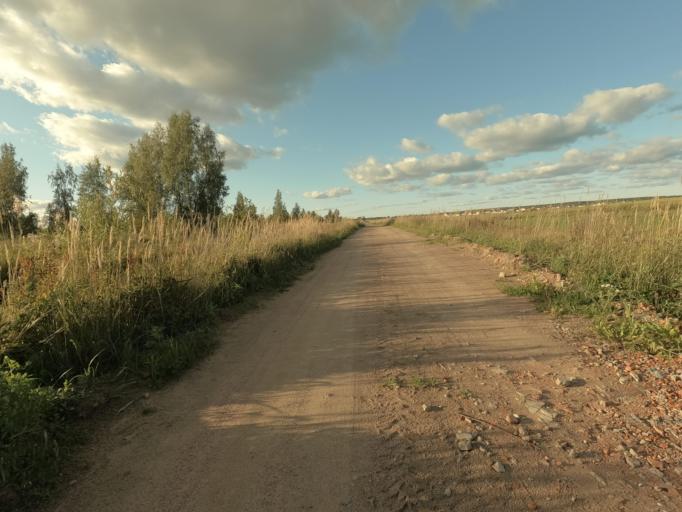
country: RU
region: Leningrad
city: Imeni Sverdlova
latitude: 59.8606
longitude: 30.7311
